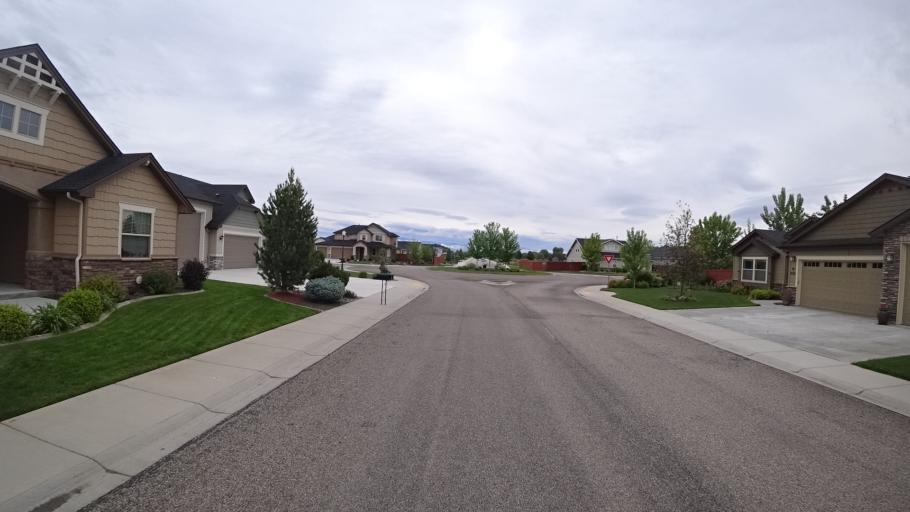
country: US
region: Idaho
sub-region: Ada County
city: Star
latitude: 43.7013
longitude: -116.4795
